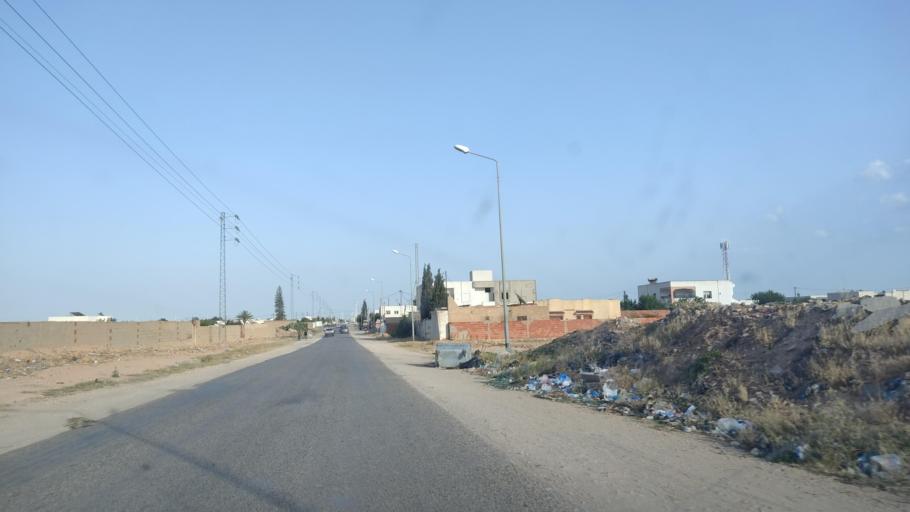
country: TN
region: Safaqis
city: Sfax
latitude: 34.8003
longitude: 10.6742
